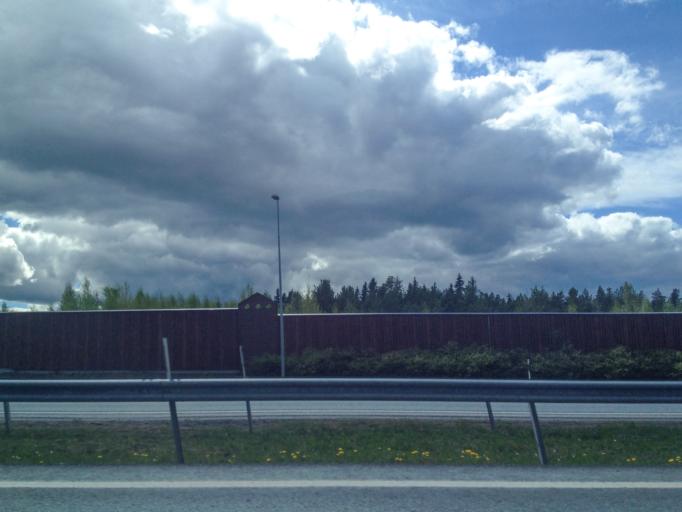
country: FI
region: Pirkanmaa
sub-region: Etelae-Pirkanmaa
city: Akaa
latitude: 61.1839
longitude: 23.8859
